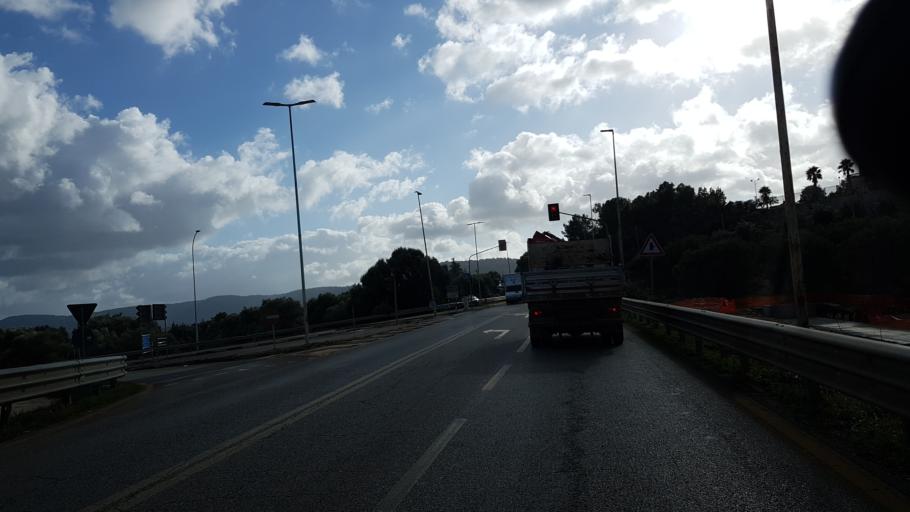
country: IT
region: Apulia
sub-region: Provincia di Brindisi
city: Fasano
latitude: 40.8303
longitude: 17.3504
